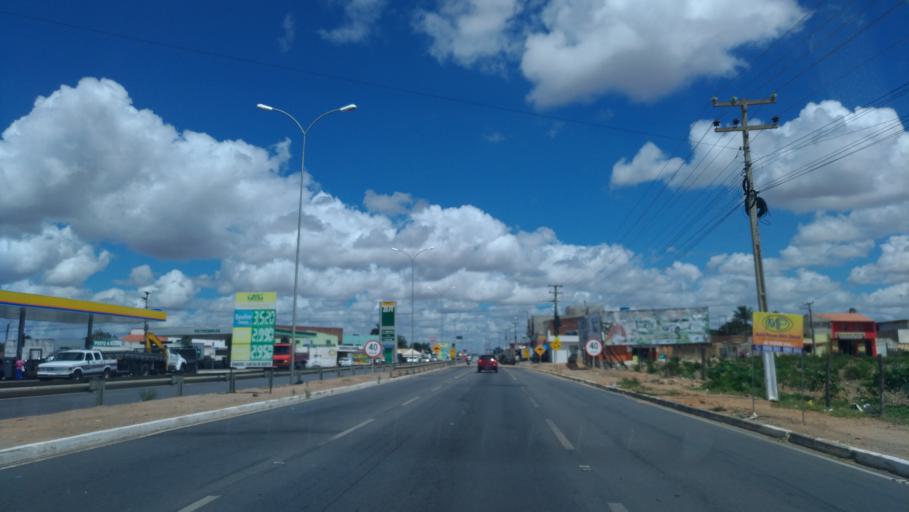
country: BR
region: Alagoas
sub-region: Arapiraca
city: Arapiraca
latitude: -9.7245
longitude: -36.6781
